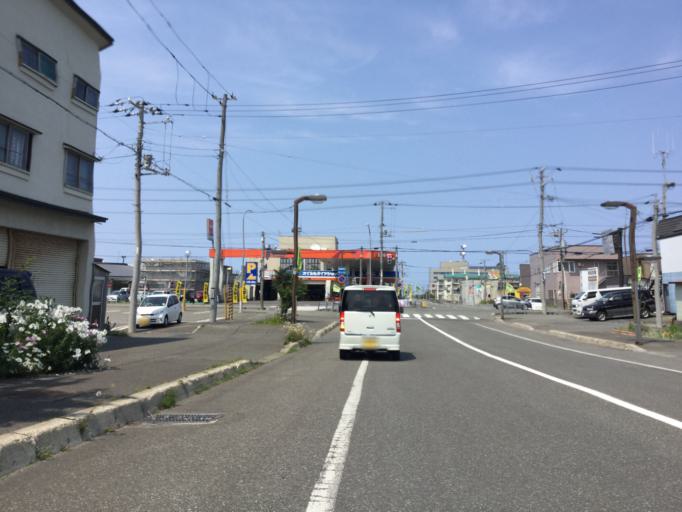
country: JP
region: Hokkaido
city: Wakkanai
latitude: 45.3951
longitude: 141.7013
